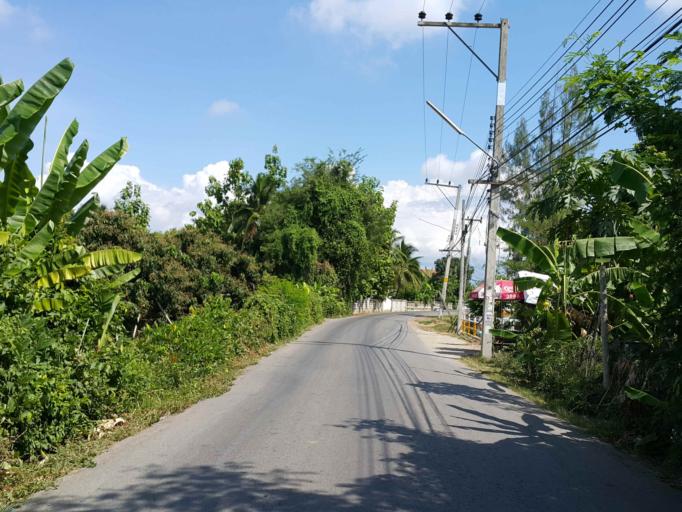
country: TH
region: Chiang Mai
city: Saraphi
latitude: 18.7245
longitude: 99.0487
